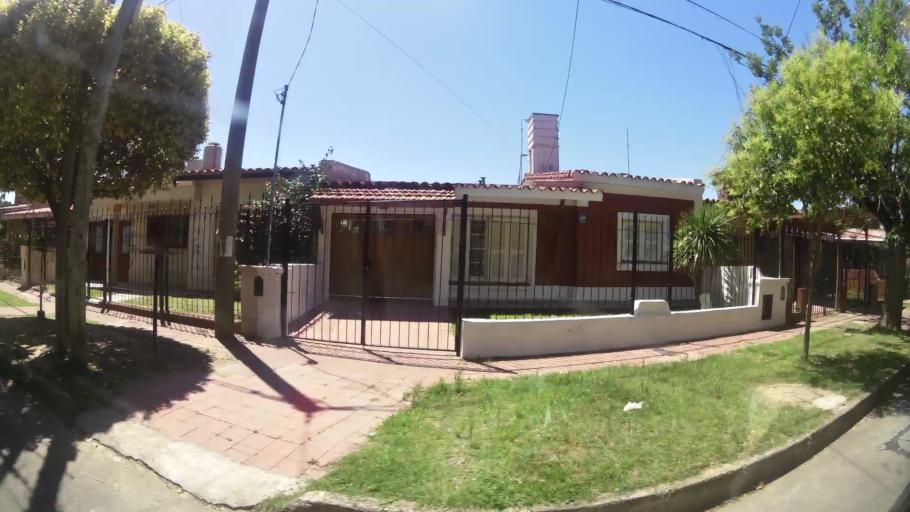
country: AR
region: Cordoba
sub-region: Departamento de Capital
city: Cordoba
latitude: -31.4342
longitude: -64.2108
